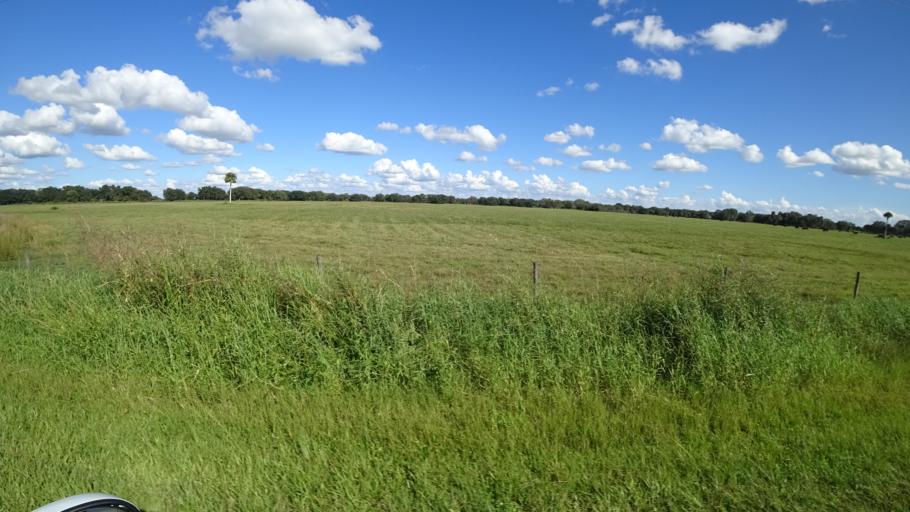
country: US
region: Florida
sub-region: Sarasota County
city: North Port
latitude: 27.1984
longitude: -82.1222
